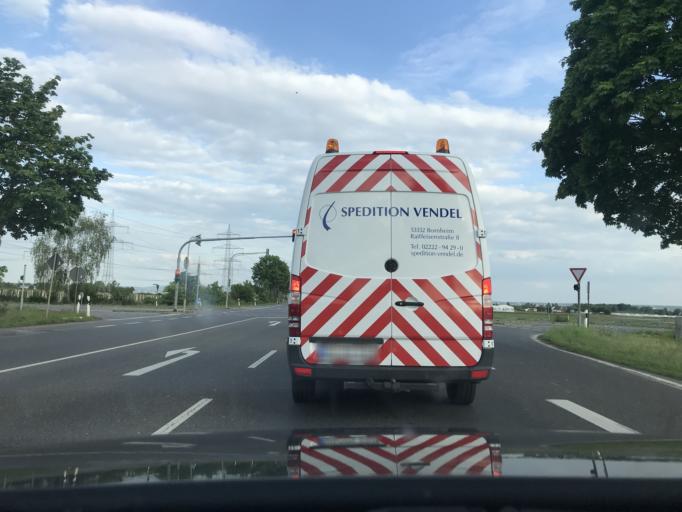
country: DE
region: North Rhine-Westphalia
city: Bornheim
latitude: 50.7688
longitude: 7.0043
